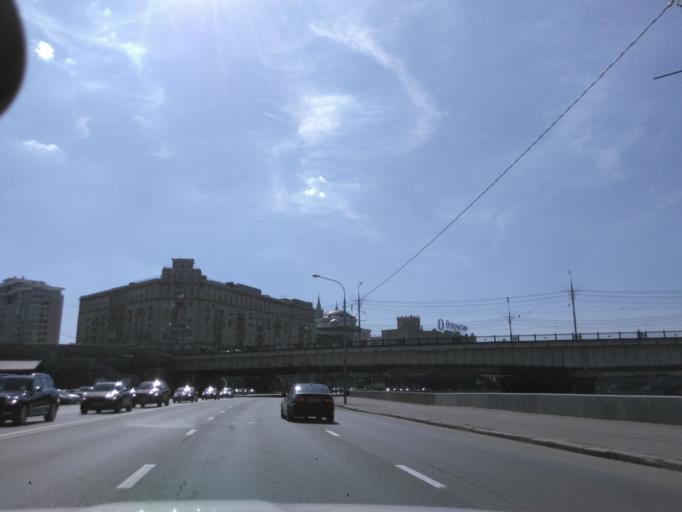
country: RU
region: Moskovskaya
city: Dorogomilovo
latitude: 55.7532
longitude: 37.5722
